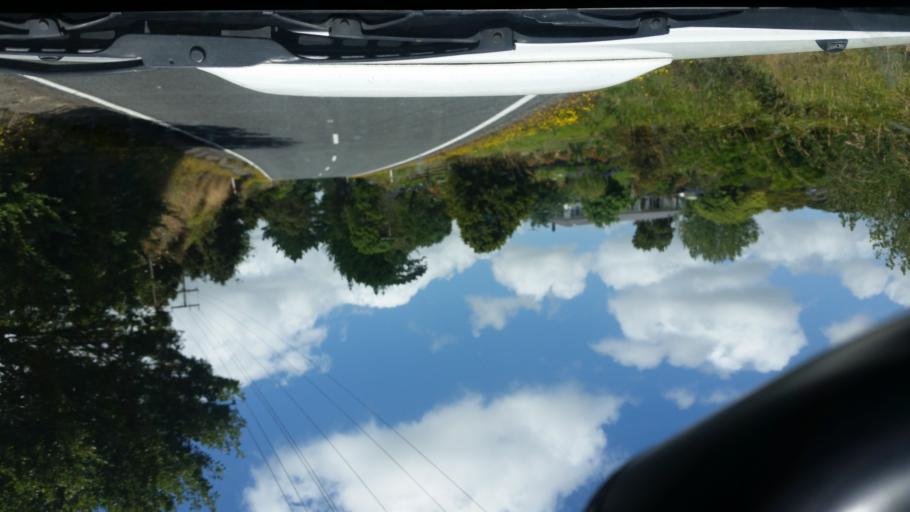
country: NZ
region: Northland
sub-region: Whangarei
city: Ruakaka
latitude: -36.0672
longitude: 174.2654
